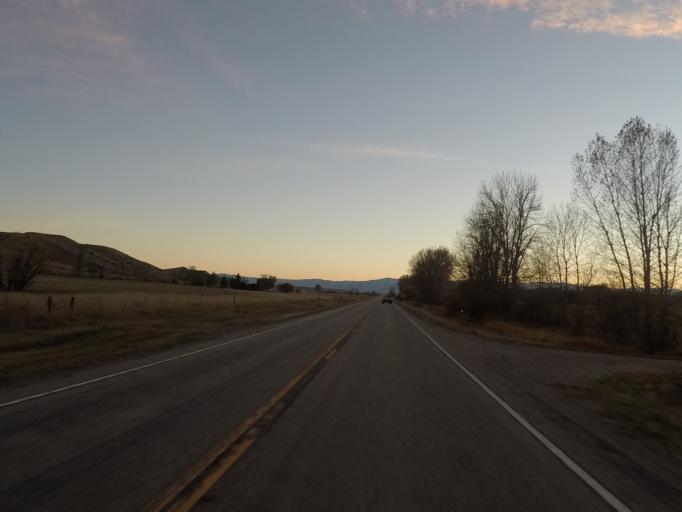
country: US
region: Montana
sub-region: Stillwater County
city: Columbus
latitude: 45.4535
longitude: -109.0752
